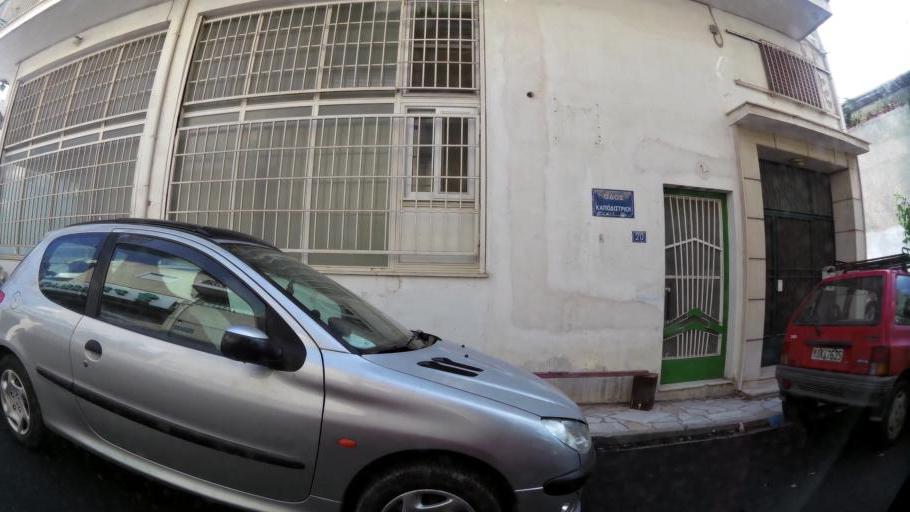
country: GR
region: Attica
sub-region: Nomarchia Dytikis Attikis
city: Zefyri
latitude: 38.0669
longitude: 23.7148
